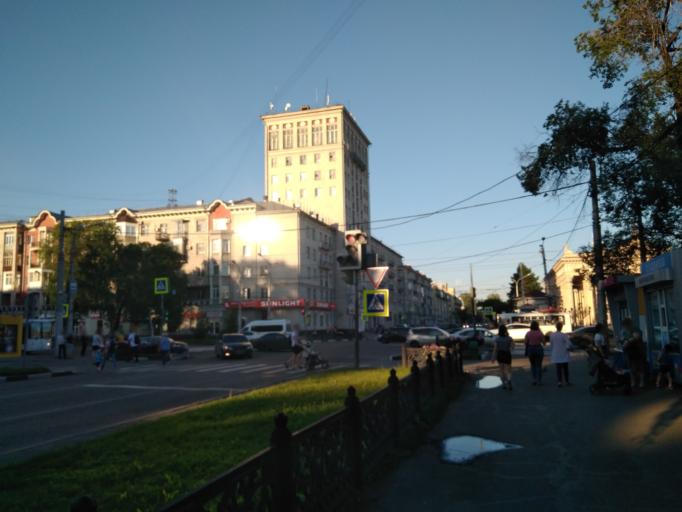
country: RU
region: Kemerovo
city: Novokuznetsk
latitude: 53.7577
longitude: 87.1177
